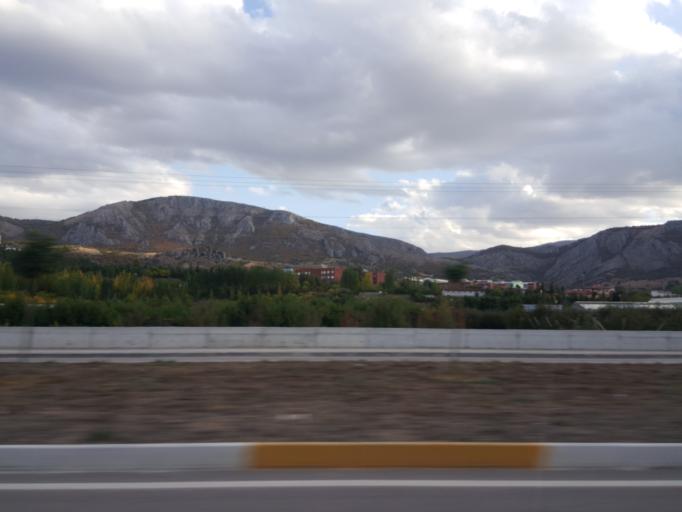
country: TR
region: Tokat
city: Tokat
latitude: 40.3347
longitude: 36.4762
